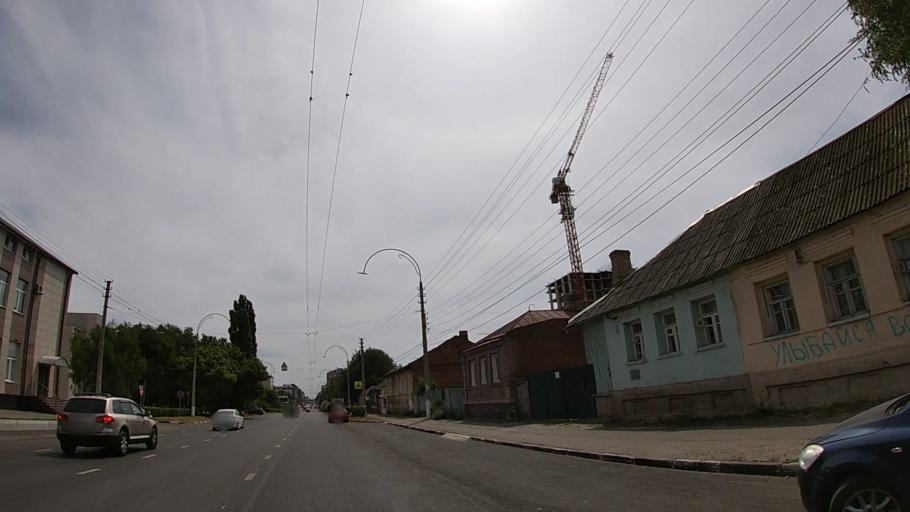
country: RU
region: Belgorod
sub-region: Belgorodskiy Rayon
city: Belgorod
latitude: 50.5995
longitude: 36.5739
